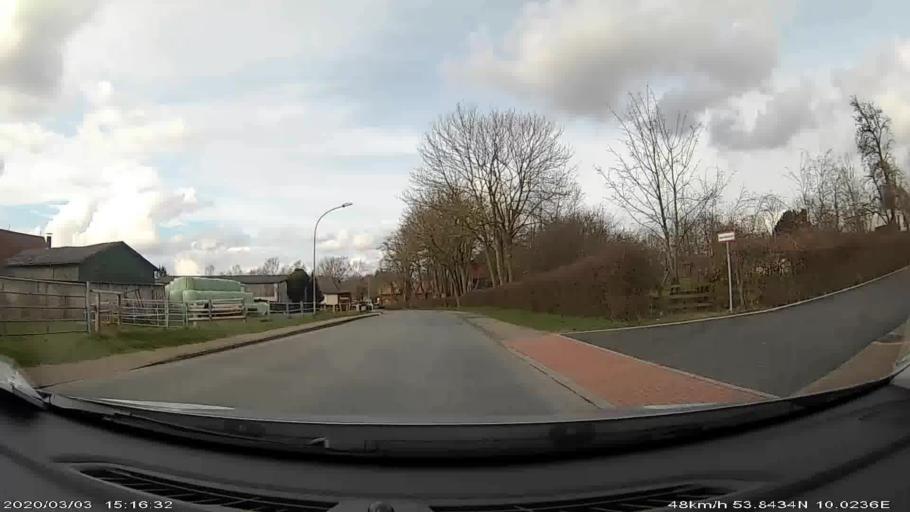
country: DE
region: Schleswig-Holstein
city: Kattendorf
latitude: 53.8424
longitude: 10.0237
